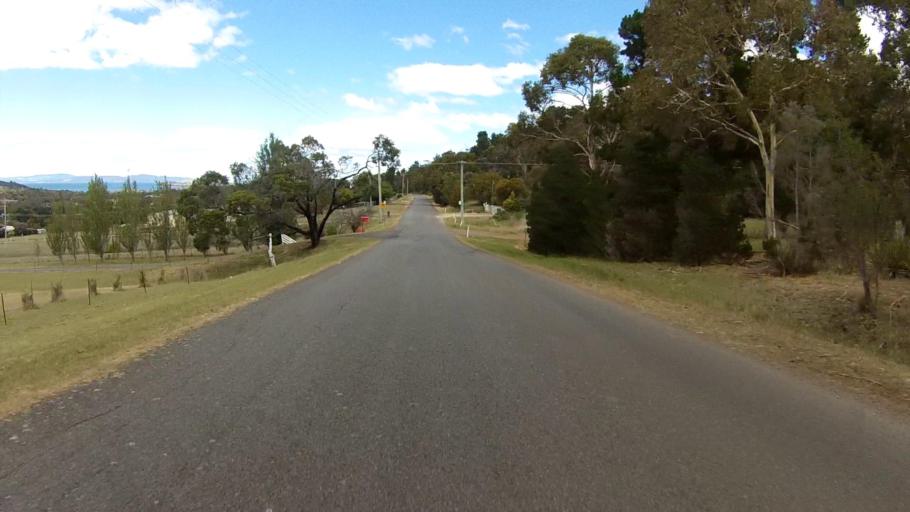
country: AU
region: Tasmania
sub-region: Clarence
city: Acton Park
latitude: -42.8647
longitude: 147.4697
